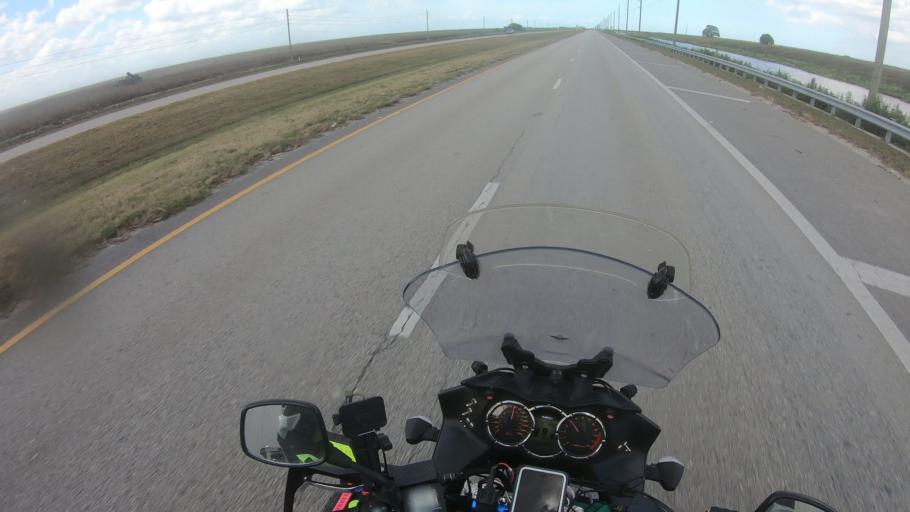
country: US
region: Florida
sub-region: Palm Beach County
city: Belle Glade Camp
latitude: 26.5901
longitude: -80.7120
